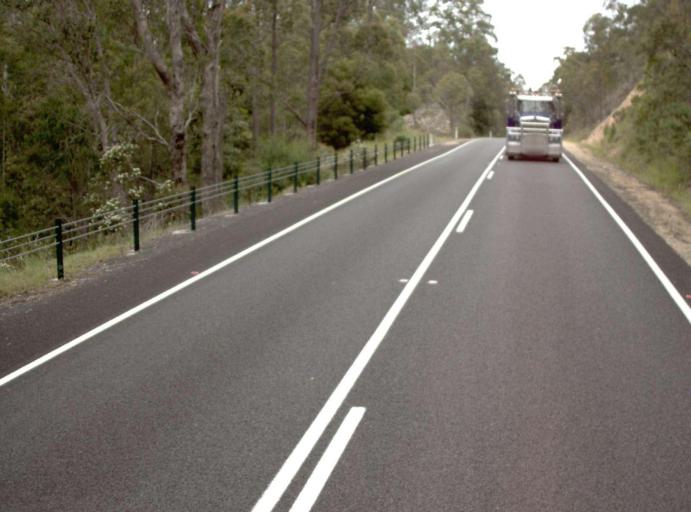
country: AU
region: New South Wales
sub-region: Bombala
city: Bombala
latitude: -37.3252
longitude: 149.2068
